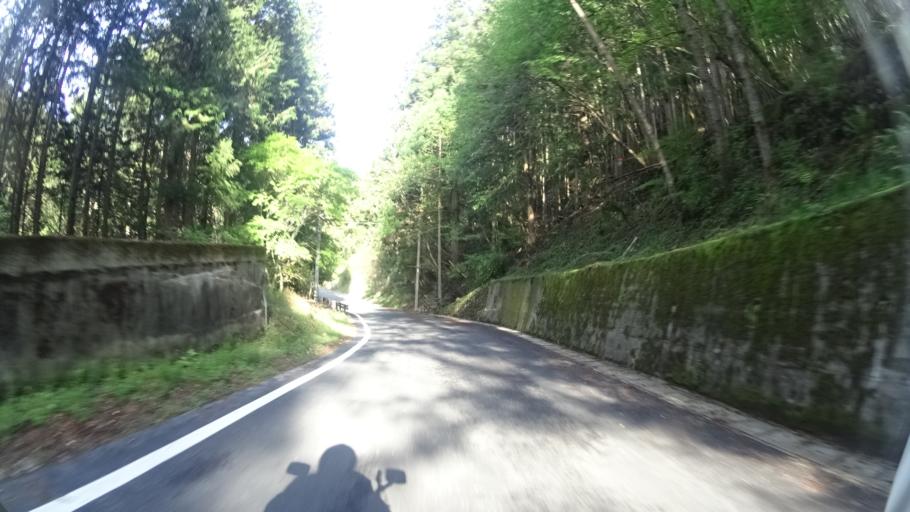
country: JP
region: Tokushima
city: Ikedacho
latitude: 33.8738
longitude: 133.9891
